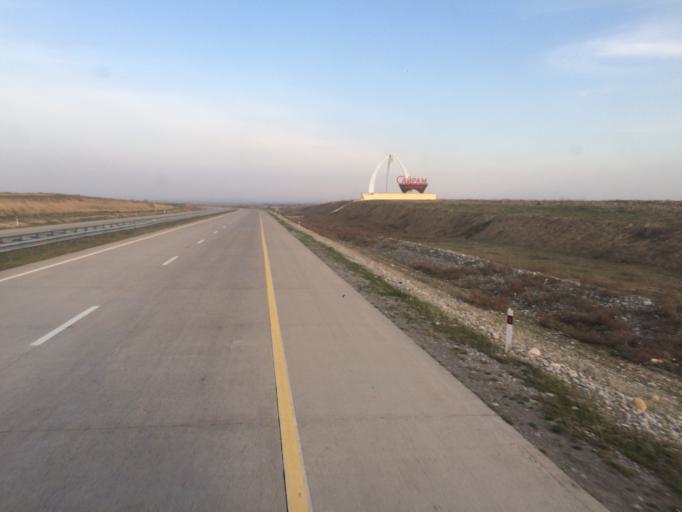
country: KZ
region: Ongtustik Qazaqstan
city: Shymkent
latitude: 42.4935
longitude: 69.4761
